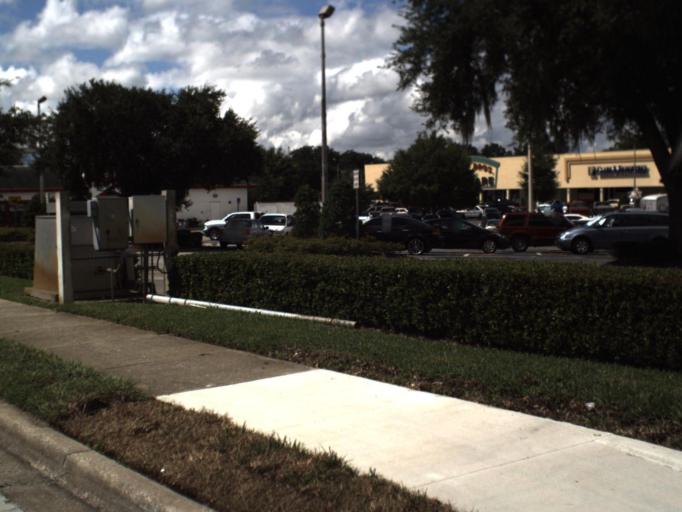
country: US
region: Florida
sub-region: Polk County
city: Lakeland
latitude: 28.0141
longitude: -81.9571
